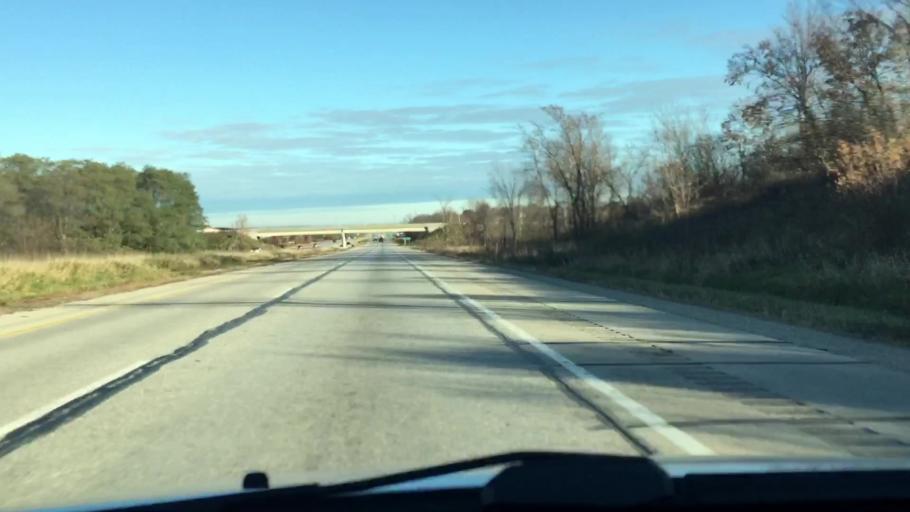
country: US
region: Wisconsin
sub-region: Fond du Lac County
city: Fond du Lac
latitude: 43.7086
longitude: -88.4421
